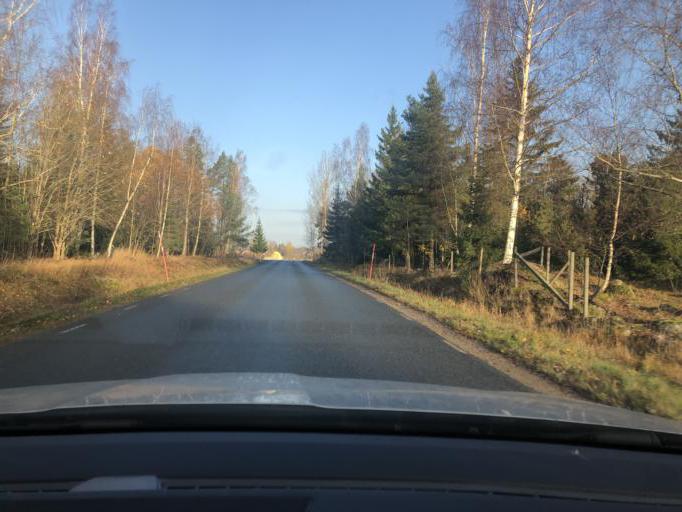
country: SE
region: Soedermanland
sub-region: Flens Kommun
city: Halleforsnas
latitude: 59.0341
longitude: 16.3960
